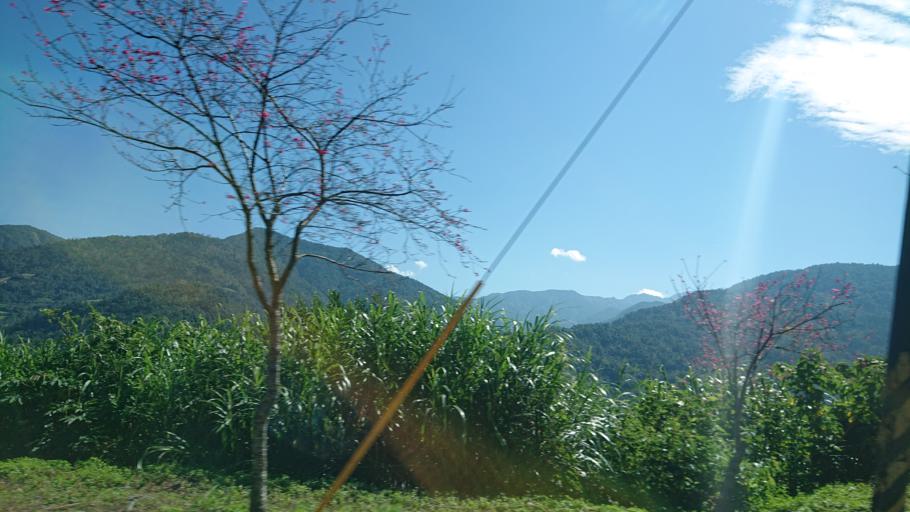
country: TW
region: Taiwan
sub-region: Yilan
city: Yilan
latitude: 24.6063
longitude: 121.5224
